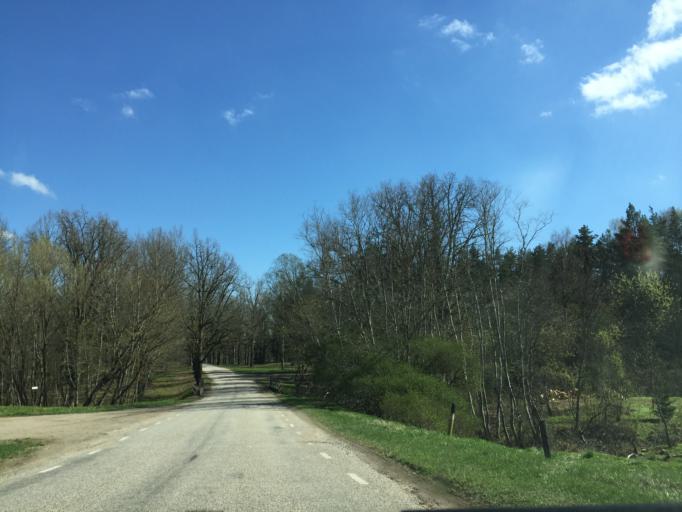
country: EE
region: Valgamaa
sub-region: Valga linn
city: Valga
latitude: 57.8533
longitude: 26.1215
